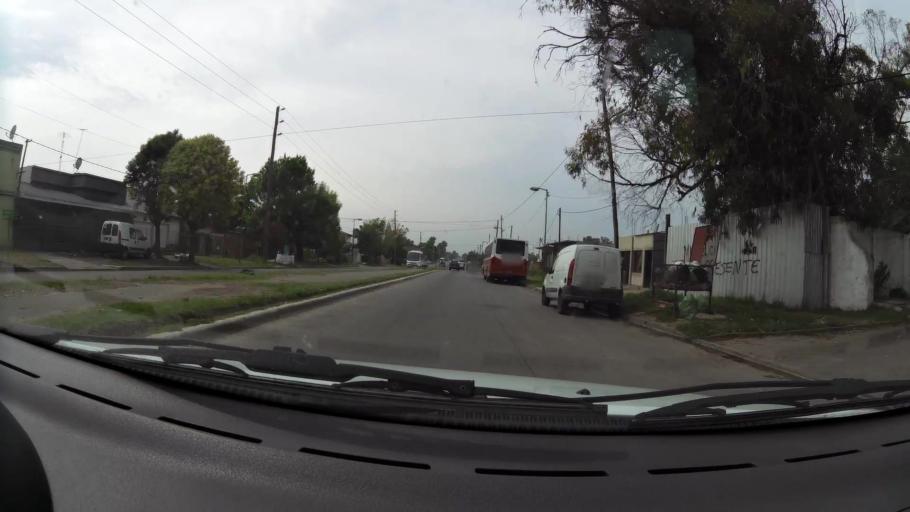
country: AR
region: Buenos Aires
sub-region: Partido de La Plata
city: La Plata
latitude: -34.9259
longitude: -58.0183
